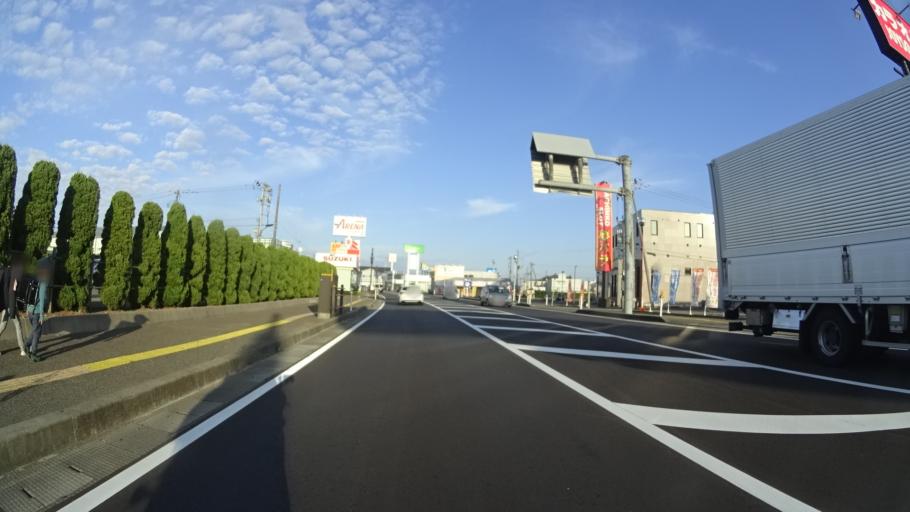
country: JP
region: Niigata
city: Kashiwazaki
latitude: 37.3611
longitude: 138.5652
